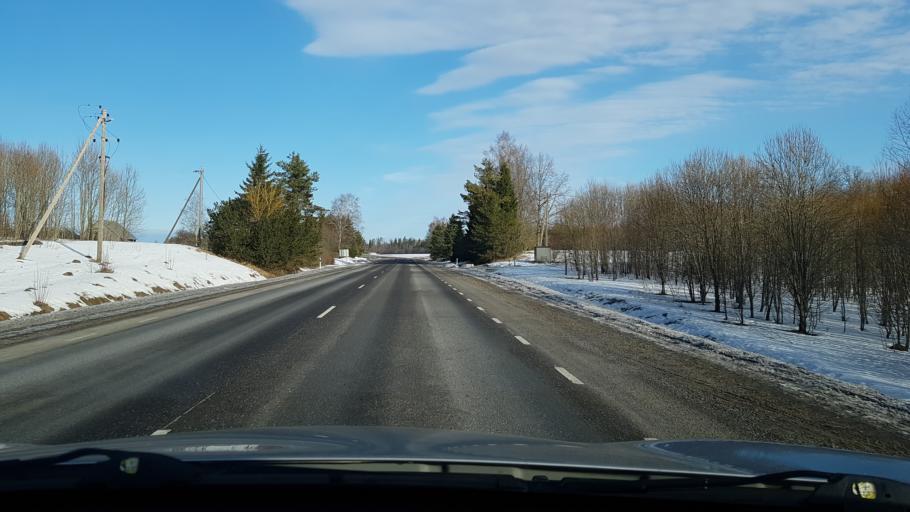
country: EE
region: Viljandimaa
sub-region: Viljandi linn
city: Viljandi
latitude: 58.4191
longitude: 25.5973
